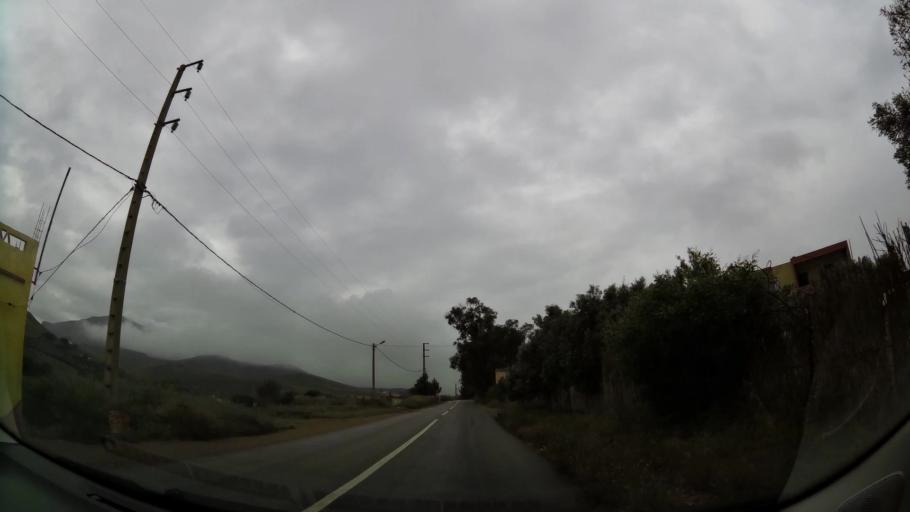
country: MA
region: Oriental
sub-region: Nador
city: Nador
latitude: 35.1432
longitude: -3.0449
